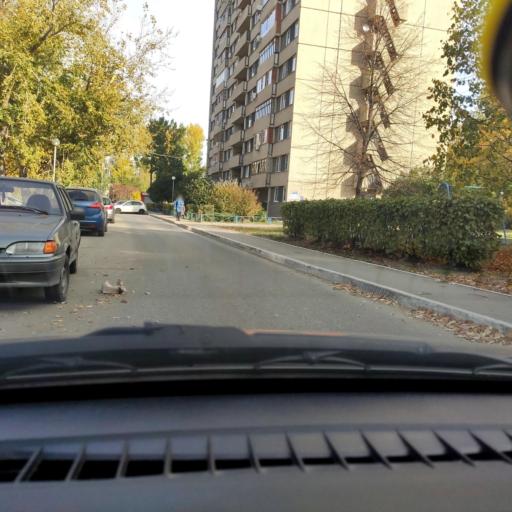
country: RU
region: Samara
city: Tol'yatti
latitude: 53.5046
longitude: 49.2871
